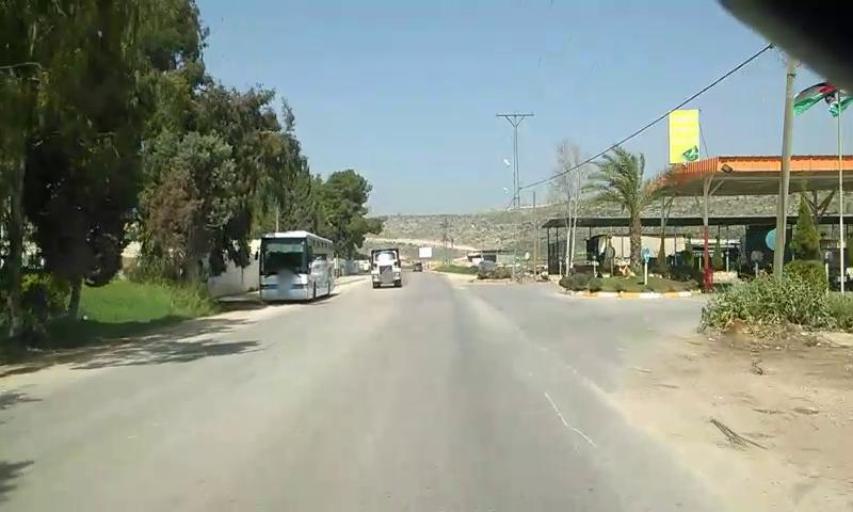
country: PS
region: West Bank
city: Az Zababidah
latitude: 32.3937
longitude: 35.3207
